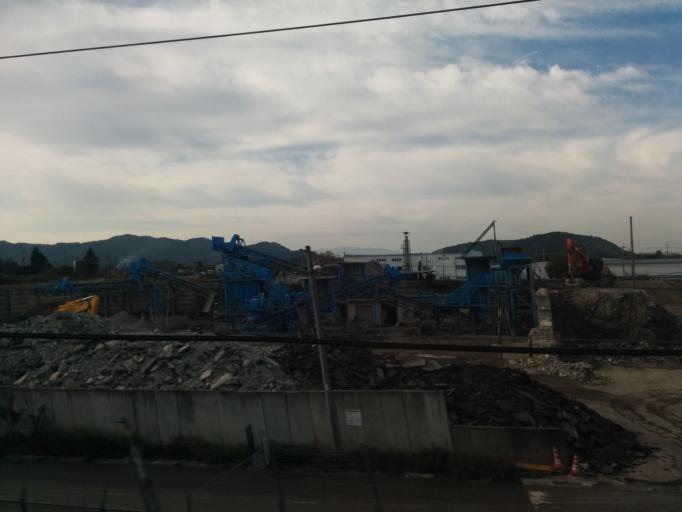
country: JP
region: Shiga Prefecture
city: Youkaichi
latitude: 35.1650
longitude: 136.2055
